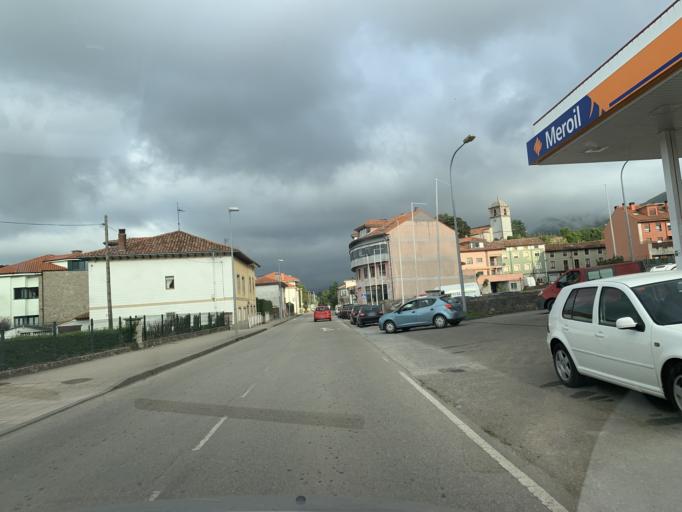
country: ES
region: Asturias
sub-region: Province of Asturias
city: Llanes
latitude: 43.4266
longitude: -4.8623
